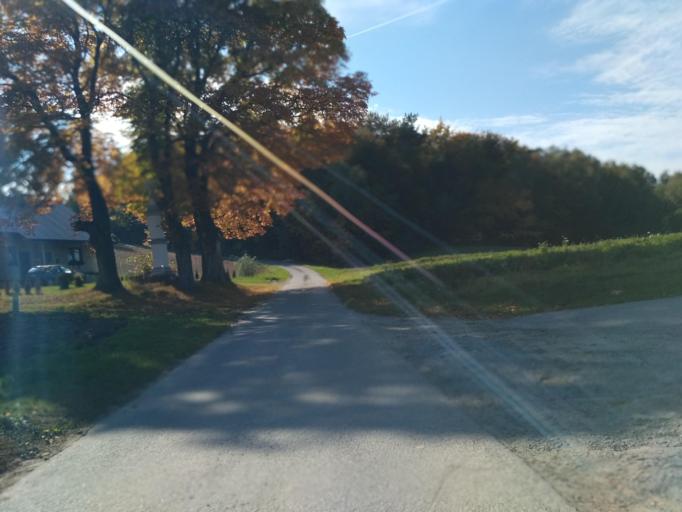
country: PL
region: Subcarpathian Voivodeship
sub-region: Powiat debicki
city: Slotowa
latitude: 49.9368
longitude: 21.2776
